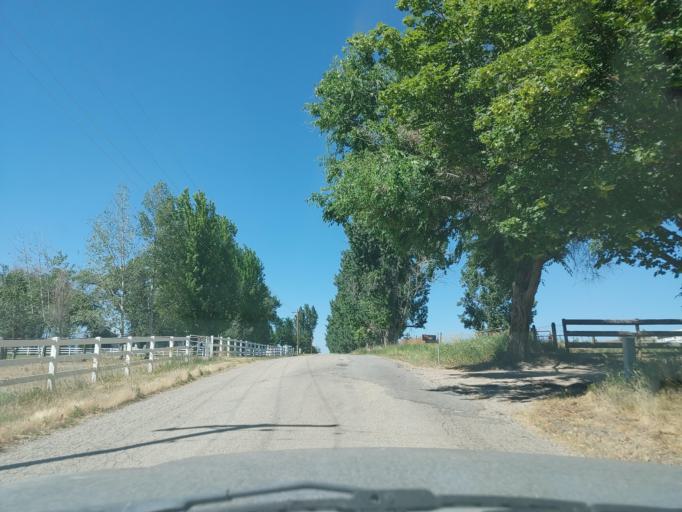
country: US
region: Montana
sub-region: Ravalli County
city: Hamilton
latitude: 46.3286
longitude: -114.0614
